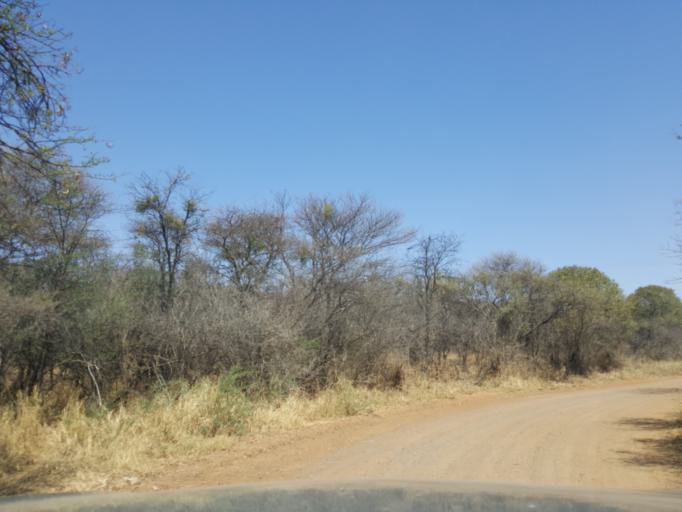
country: BW
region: South East
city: Lobatse
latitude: -25.1571
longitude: 25.6887
